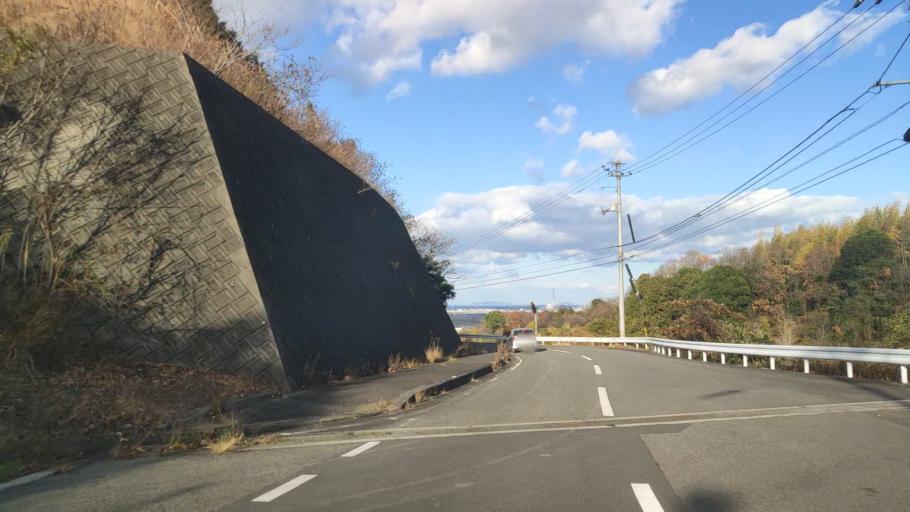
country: JP
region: Ehime
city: Saijo
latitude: 33.8843
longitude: 133.1303
